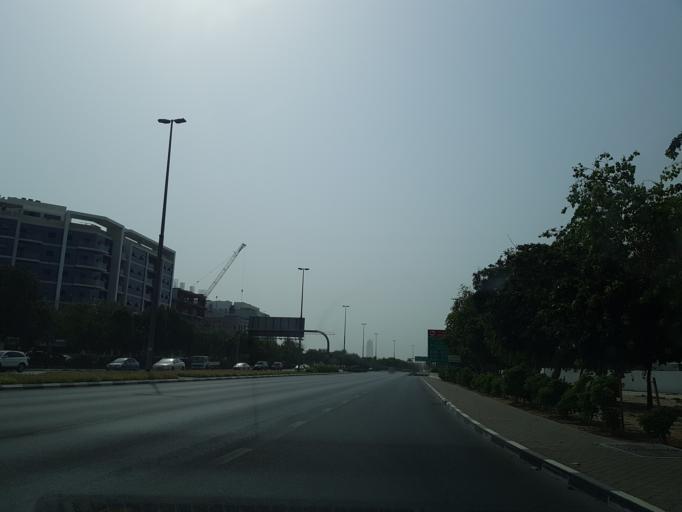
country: AE
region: Ash Shariqah
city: Sharjah
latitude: 25.2493
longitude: 55.2809
